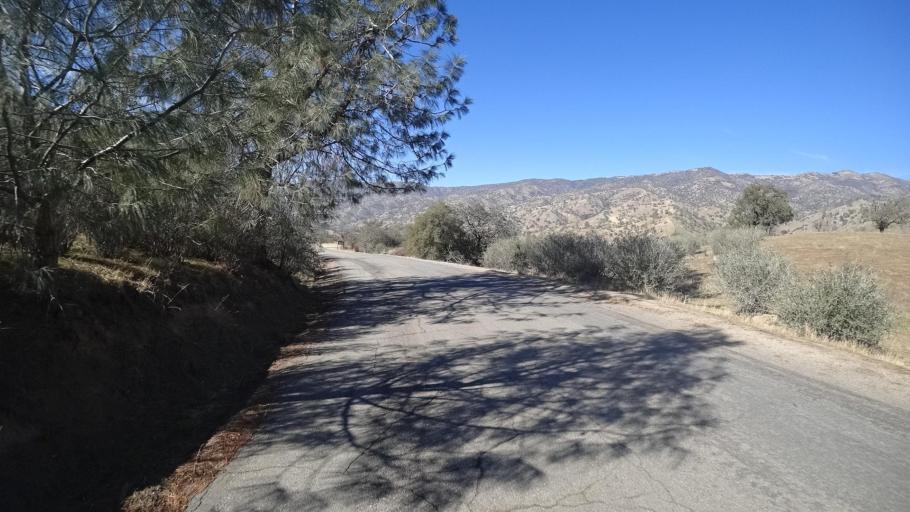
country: US
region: California
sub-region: Kern County
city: Bodfish
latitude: 35.5346
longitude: -118.6309
